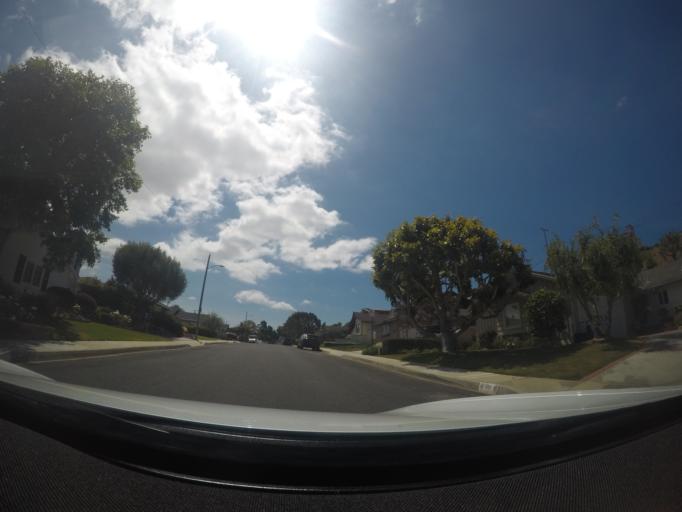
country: US
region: California
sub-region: Los Angeles County
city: Palos Verdes Estates
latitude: 33.8068
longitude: -118.3704
